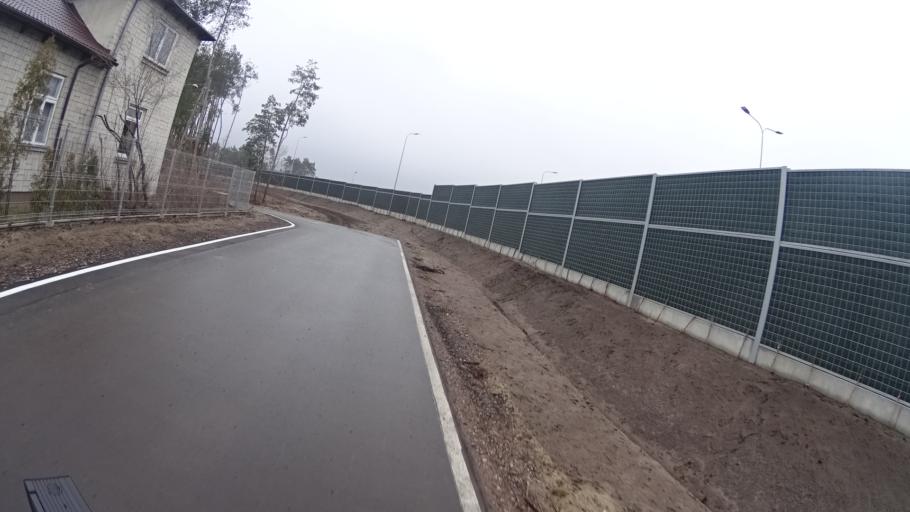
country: PL
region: Masovian Voivodeship
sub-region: Warszawa
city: Wawer
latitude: 52.1680
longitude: 21.1982
